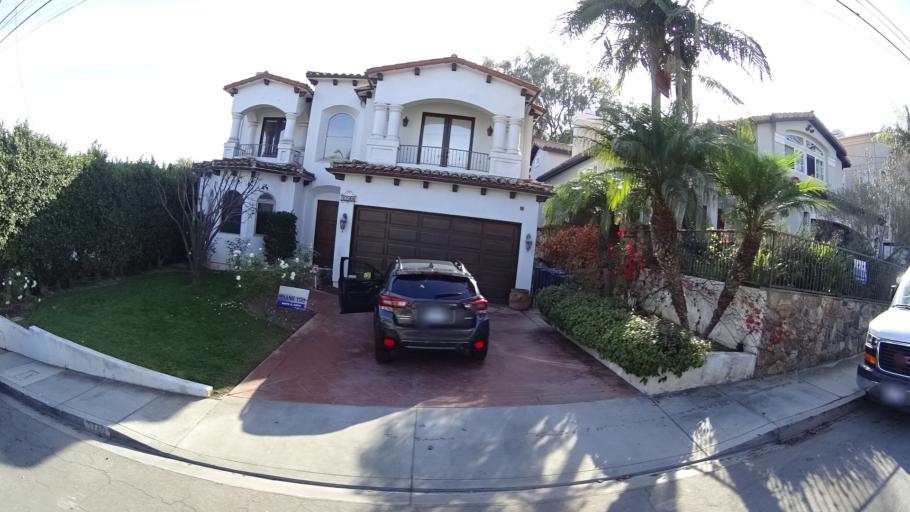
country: US
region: California
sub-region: Los Angeles County
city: Hermosa Beach
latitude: 33.8756
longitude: -118.3816
